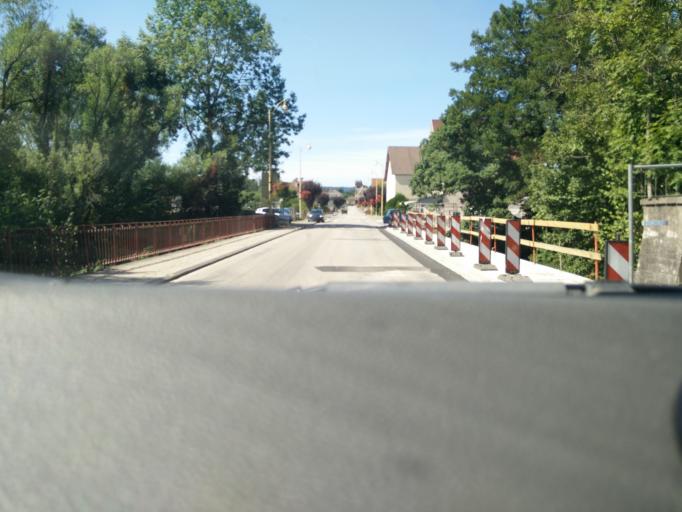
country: FR
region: Lorraine
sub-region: Departement des Vosges
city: Etival-Clairefontaine
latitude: 48.3651
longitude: 6.8744
